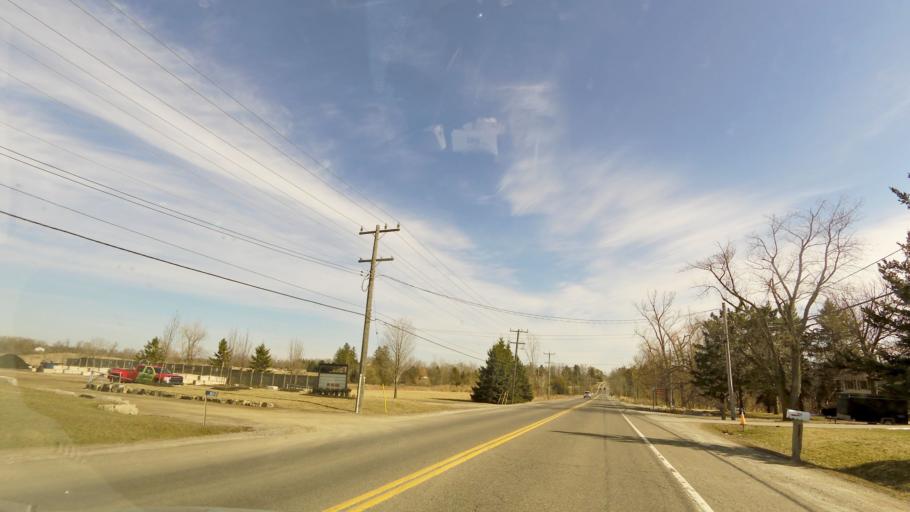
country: CA
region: Ontario
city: Burlington
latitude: 43.3539
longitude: -79.9264
